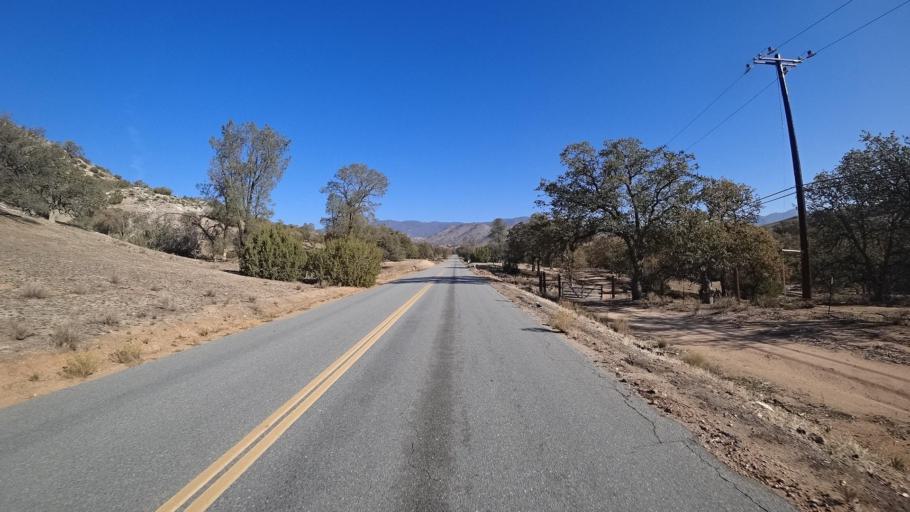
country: US
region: California
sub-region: Kern County
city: Tehachapi
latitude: 35.3354
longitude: -118.3906
